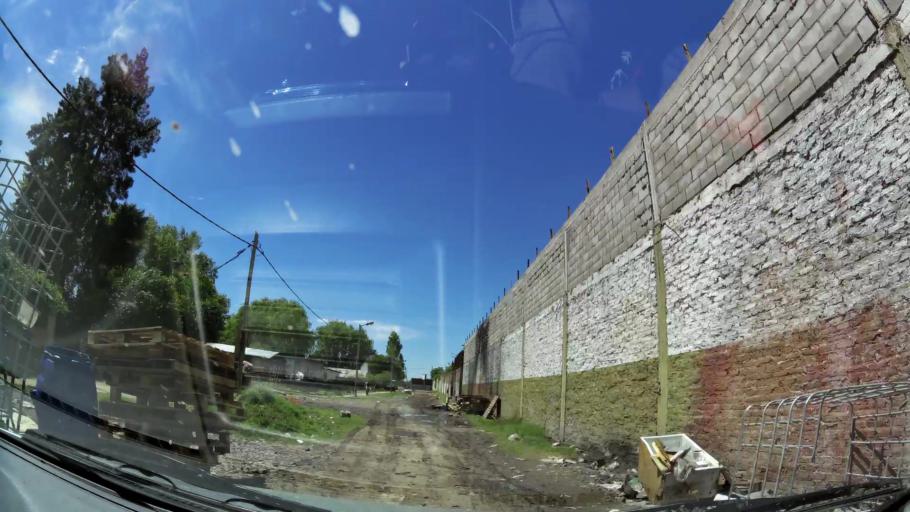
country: AR
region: Buenos Aires
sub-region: Partido de Quilmes
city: Quilmes
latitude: -34.7498
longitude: -58.3095
